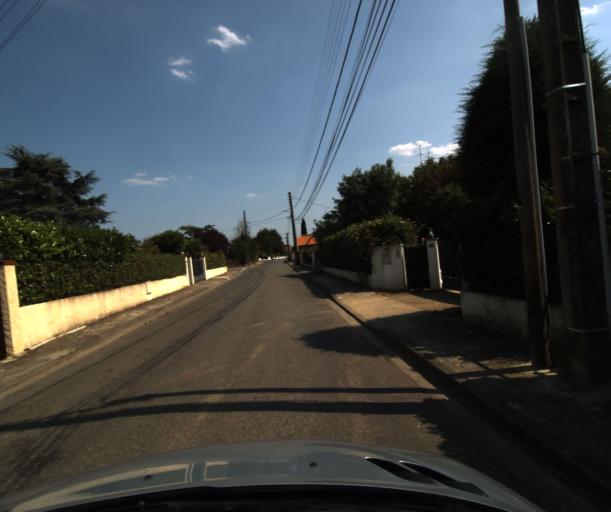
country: FR
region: Midi-Pyrenees
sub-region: Departement de la Haute-Garonne
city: Saint-Lys
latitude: 43.5059
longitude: 1.1711
